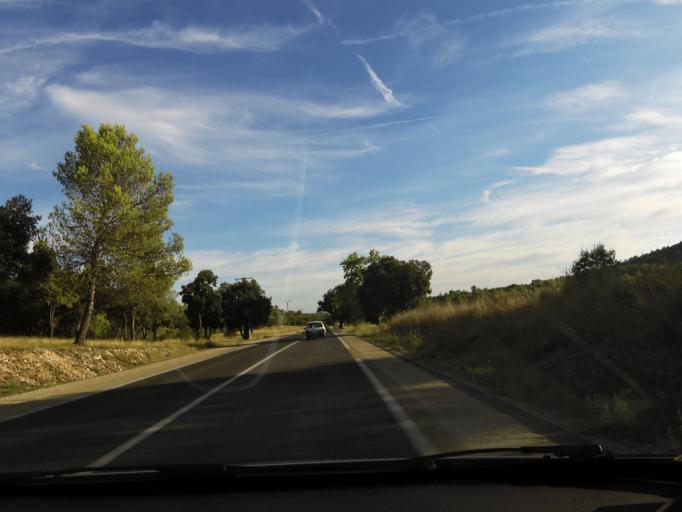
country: FR
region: Languedoc-Roussillon
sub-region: Departement de l'Herault
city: Saint-Mathieu-de-Treviers
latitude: 43.7978
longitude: 3.8766
